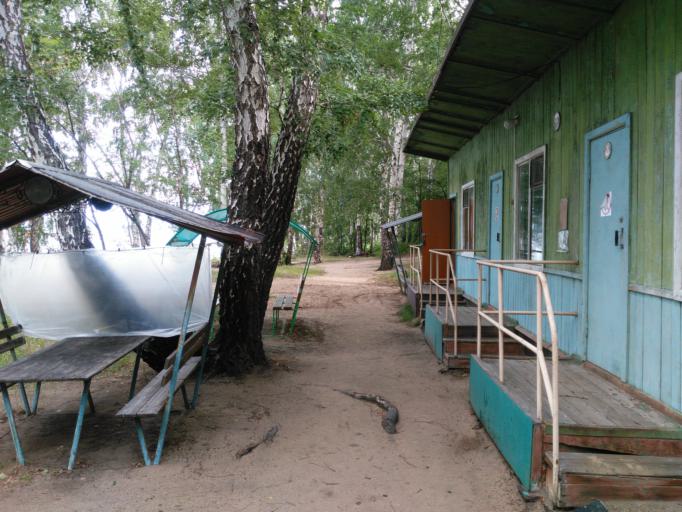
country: RU
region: Chelyabinsk
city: Tayginka
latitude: 55.4796
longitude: 60.4981
